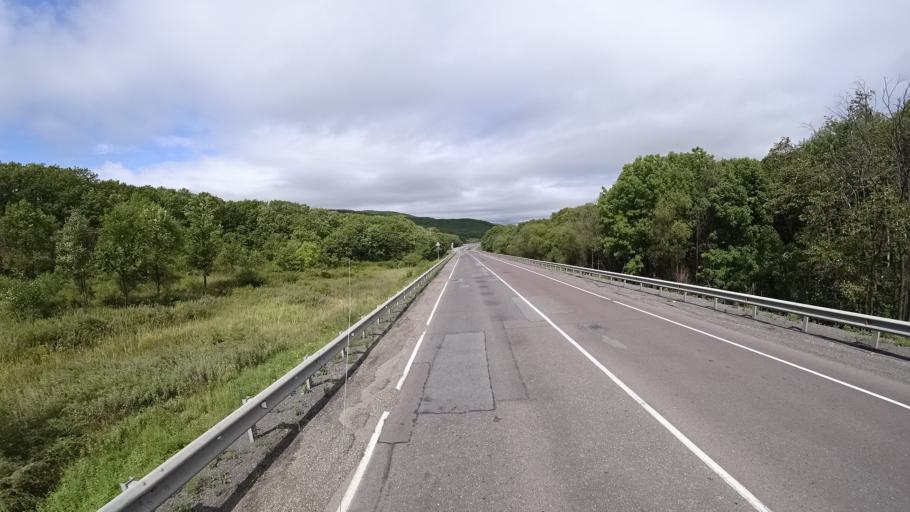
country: RU
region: Primorskiy
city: Lyalichi
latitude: 44.1347
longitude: 132.4276
